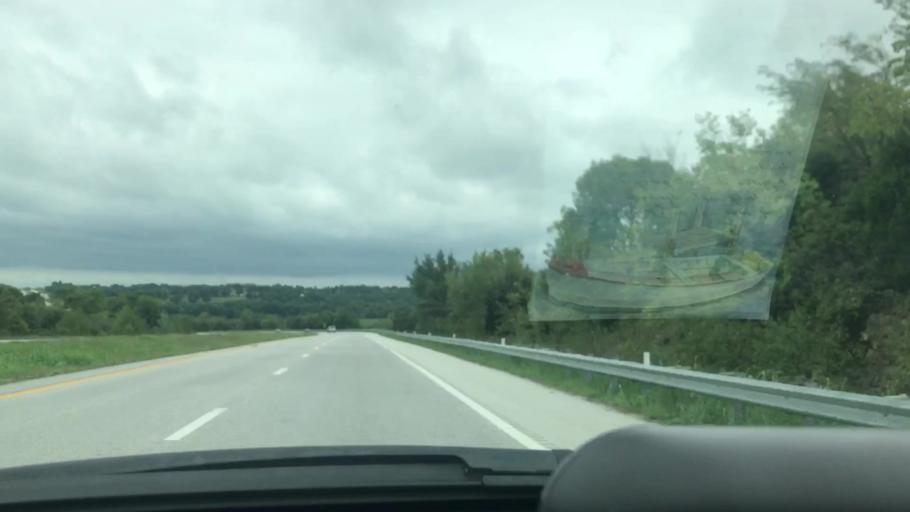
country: US
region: Missouri
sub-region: Greene County
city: Fair Grove
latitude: 37.4055
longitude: -93.1469
